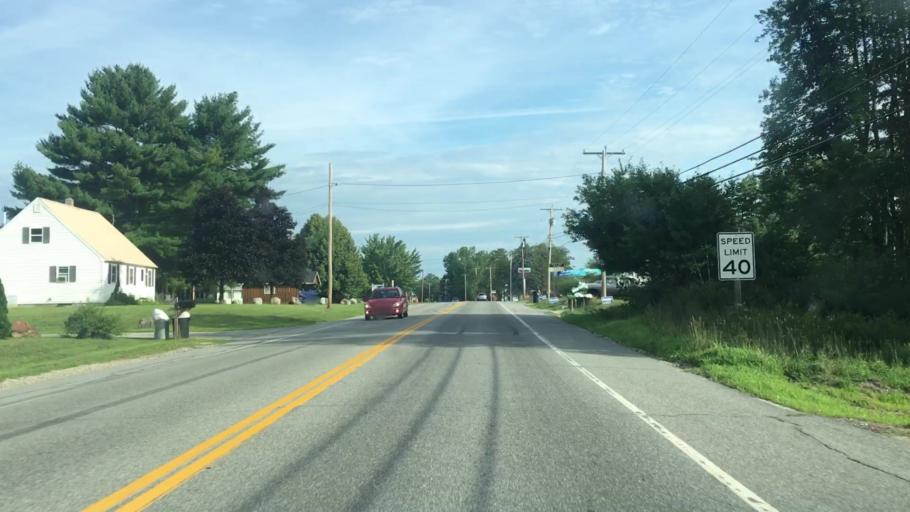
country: US
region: Maine
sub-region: York County
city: Limington
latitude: 43.7423
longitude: -70.6752
